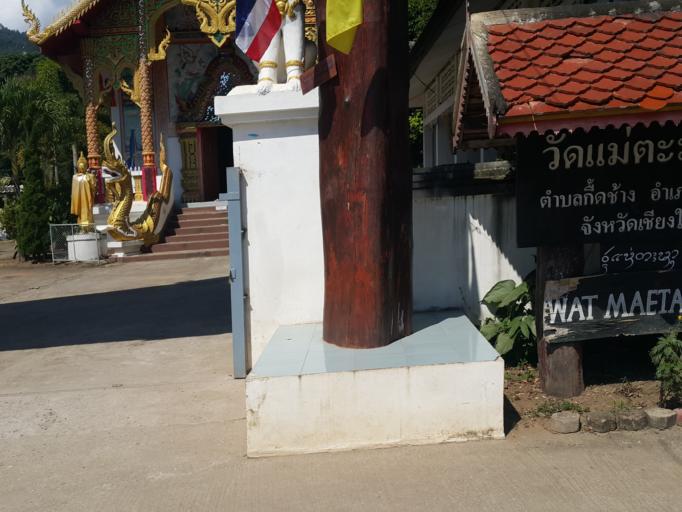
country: TH
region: Chiang Mai
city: Mae Taeng
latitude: 19.2007
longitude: 98.8871
